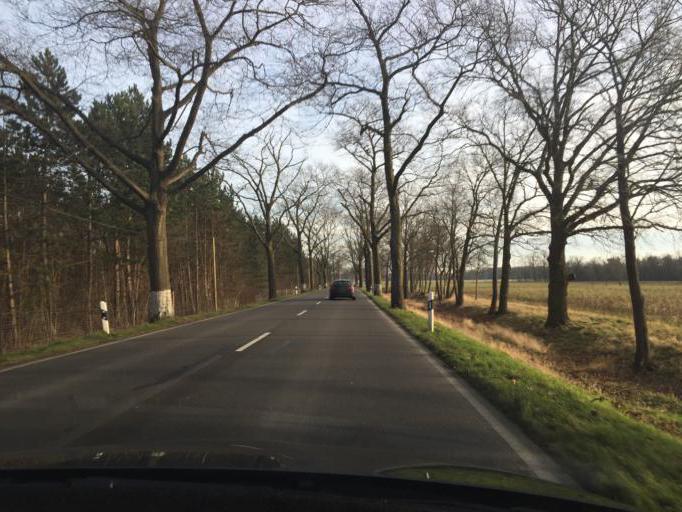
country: DE
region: Brandenburg
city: Cottbus
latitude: 51.7496
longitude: 14.3704
